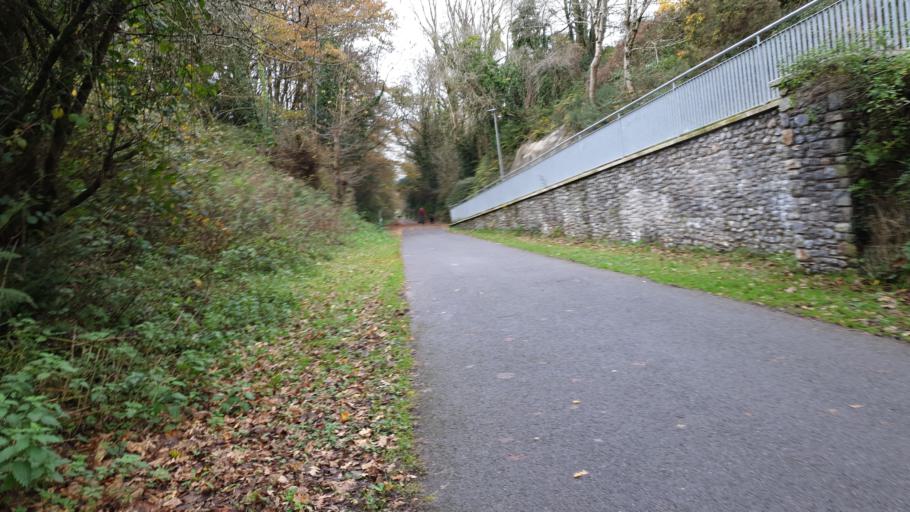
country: IE
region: Munster
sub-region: County Cork
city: Cork
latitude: 51.8872
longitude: -8.4084
